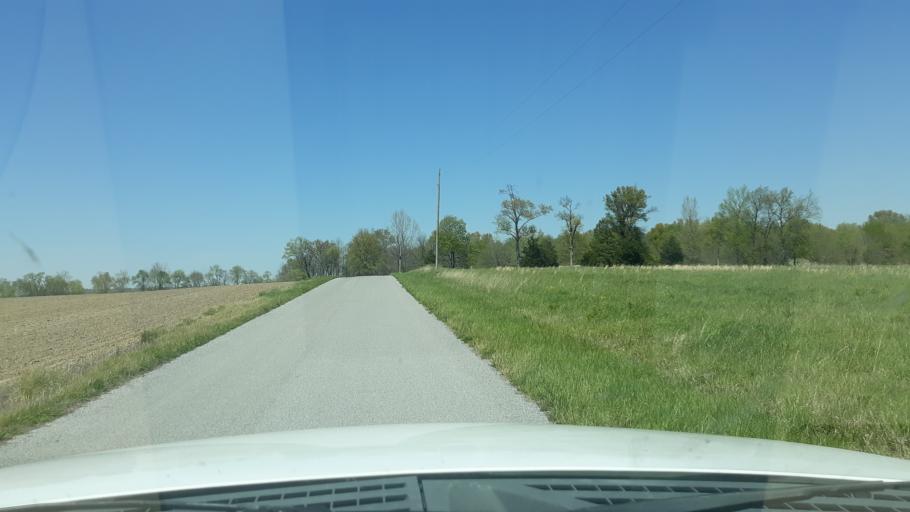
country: US
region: Illinois
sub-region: Saline County
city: Harrisburg
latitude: 37.8908
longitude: -88.6698
